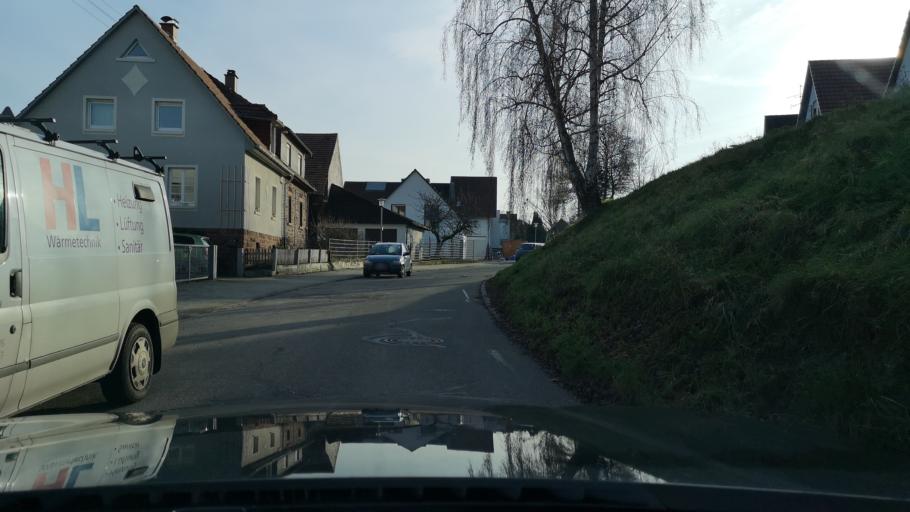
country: DE
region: Baden-Wuerttemberg
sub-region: Karlsruhe Region
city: Ettlingen
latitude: 48.9542
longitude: 8.4689
